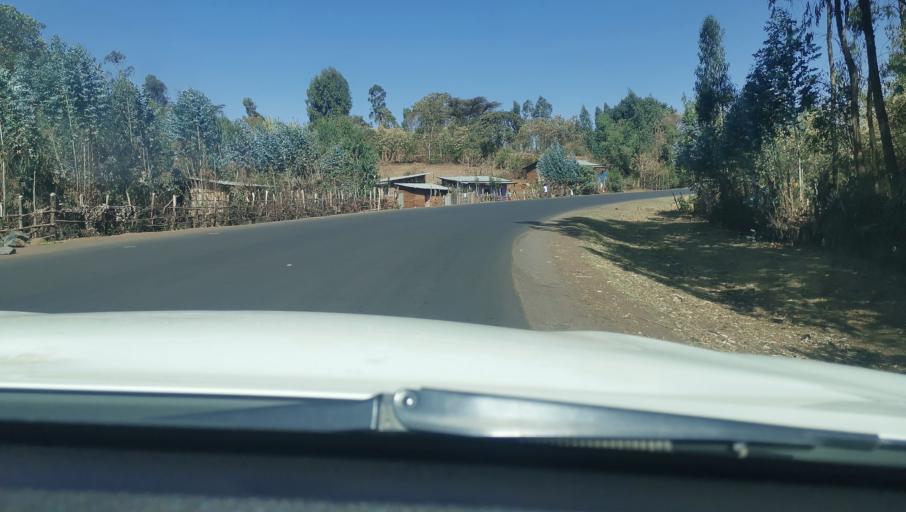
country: ET
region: Oromiya
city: Gedo
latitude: 8.9658
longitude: 37.5234
